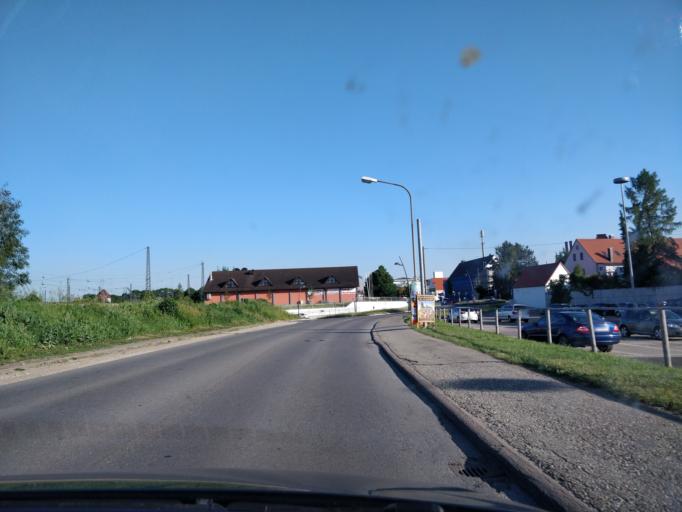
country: DE
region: Bavaria
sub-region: Swabia
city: Noerdlingen
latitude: 48.8534
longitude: 10.4961
